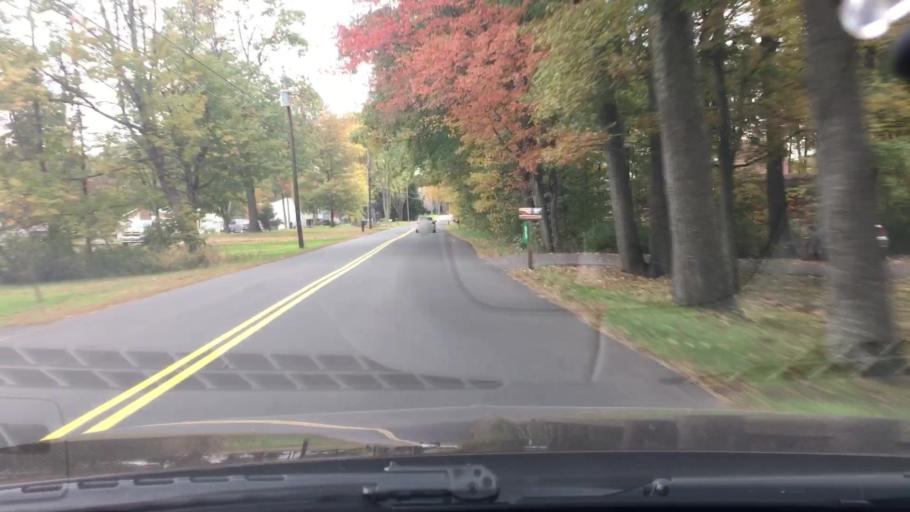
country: US
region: Connecticut
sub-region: Tolland County
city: Ellington
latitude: 41.9429
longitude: -72.4803
